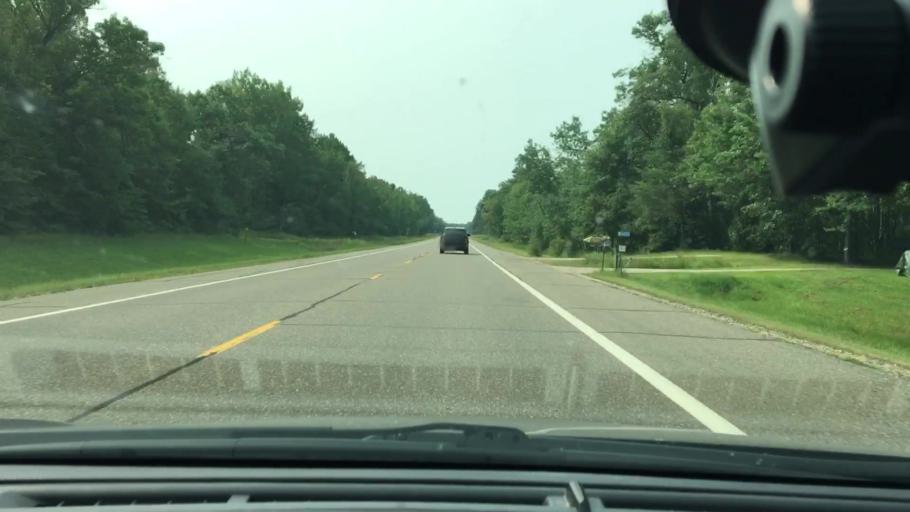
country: US
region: Minnesota
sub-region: Crow Wing County
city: Breezy Point
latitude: 46.5086
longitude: -94.1366
